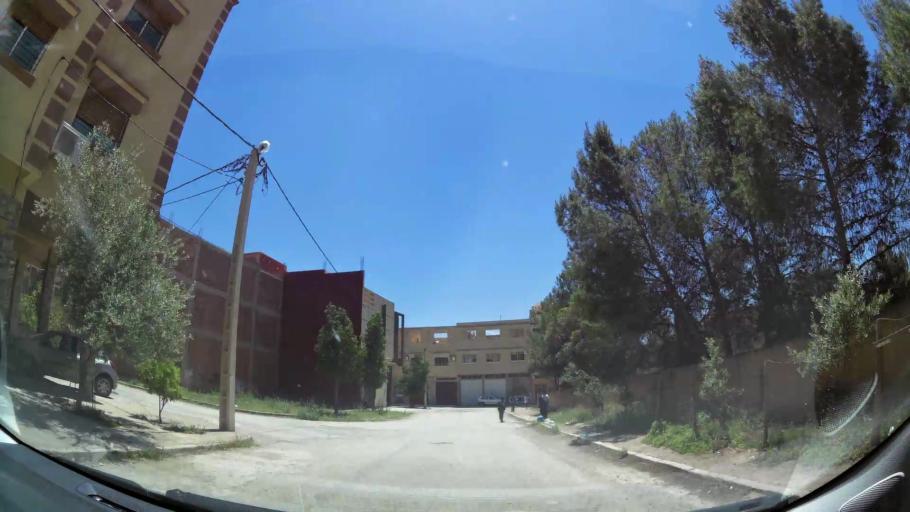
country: MA
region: Oriental
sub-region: Oujda-Angad
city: Oujda
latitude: 34.6766
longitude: -1.8726
